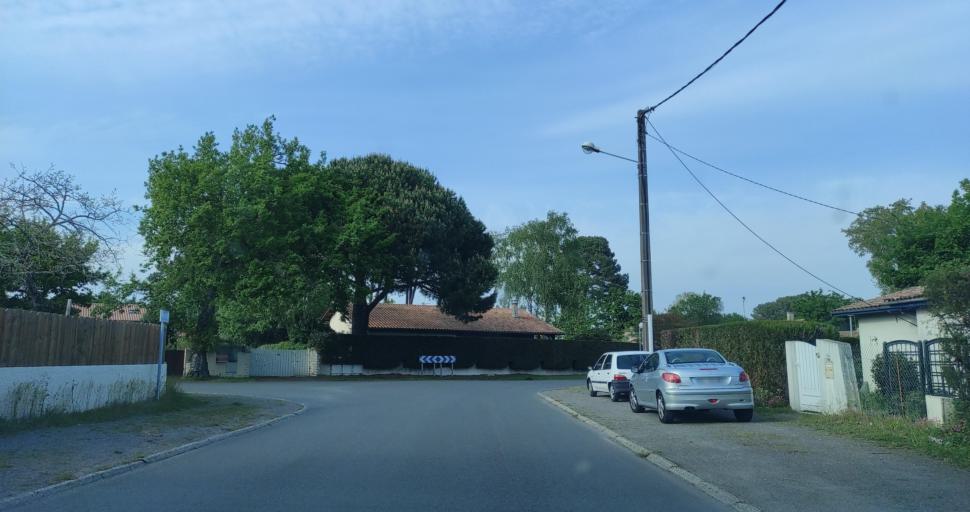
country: FR
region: Aquitaine
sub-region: Departement de la Gironde
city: Ares
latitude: 44.7638
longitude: -1.1277
